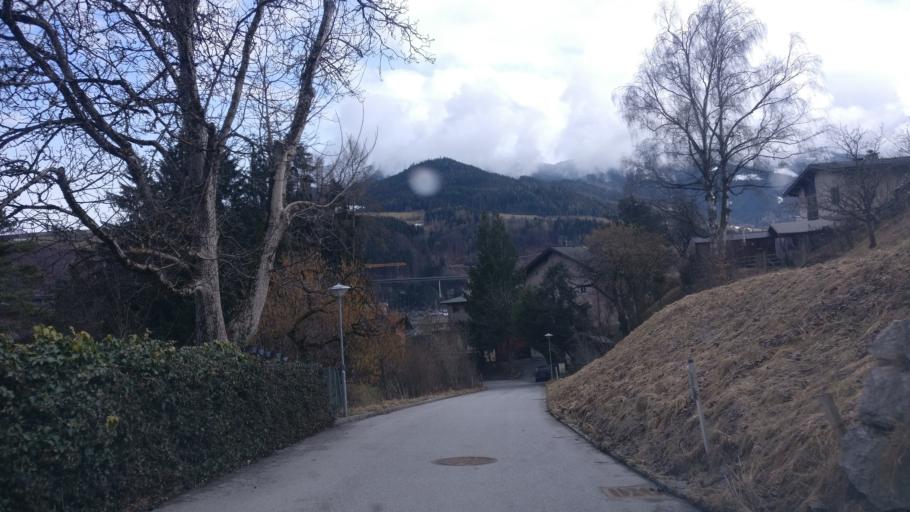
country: AT
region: Salzburg
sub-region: Politischer Bezirk Sankt Johann im Pongau
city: Bischofshofen
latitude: 47.4208
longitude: 13.2120
